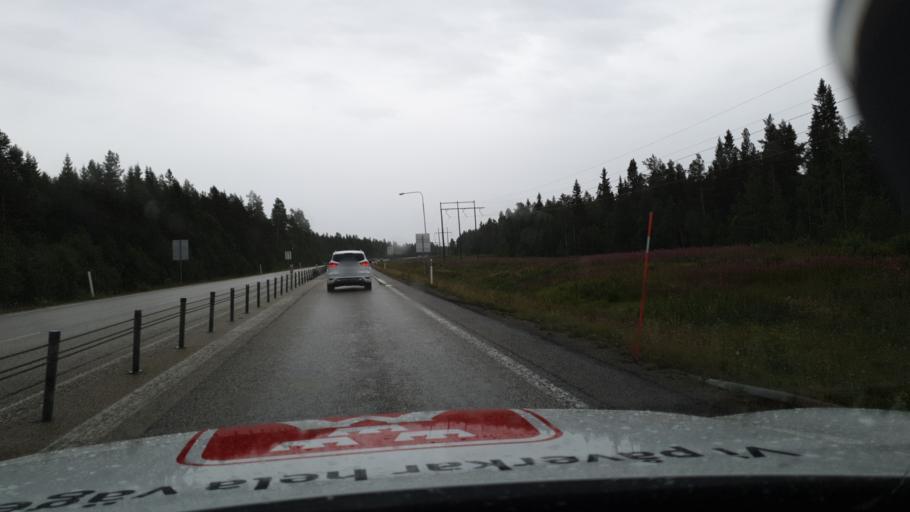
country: SE
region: Jaemtland
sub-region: OEstersunds Kommun
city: Brunflo
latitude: 63.1582
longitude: 14.7581
